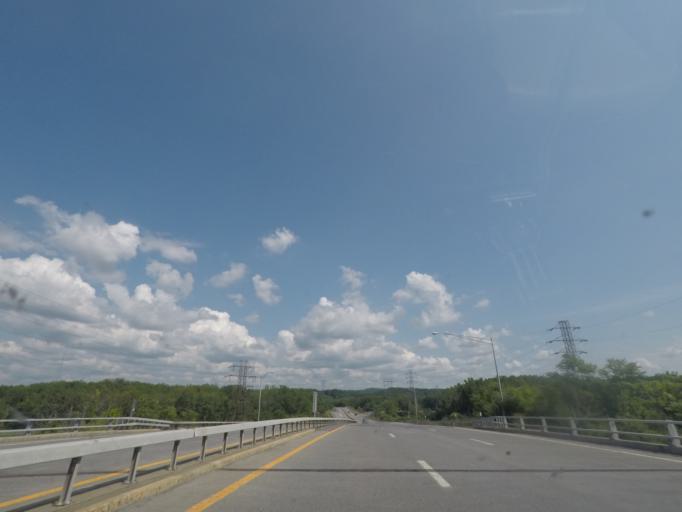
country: US
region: New York
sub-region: Albany County
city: Menands
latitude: 42.6848
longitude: -73.7285
